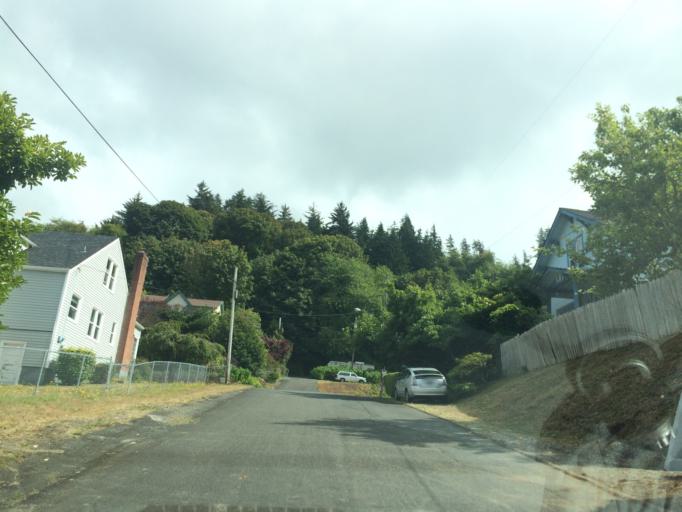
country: US
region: Oregon
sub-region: Clatsop County
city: Astoria
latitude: 46.1892
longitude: -123.8095
